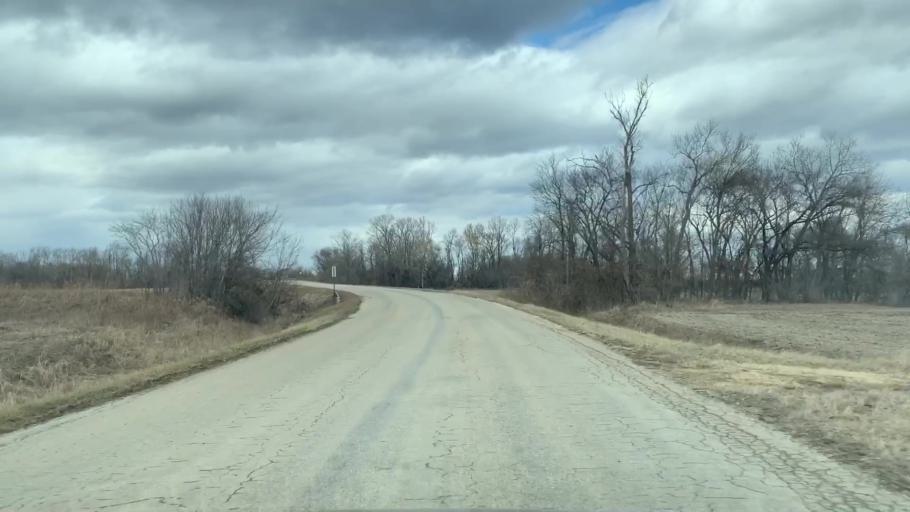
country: US
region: Kansas
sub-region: Allen County
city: Humboldt
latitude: 37.8017
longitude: -95.4705
